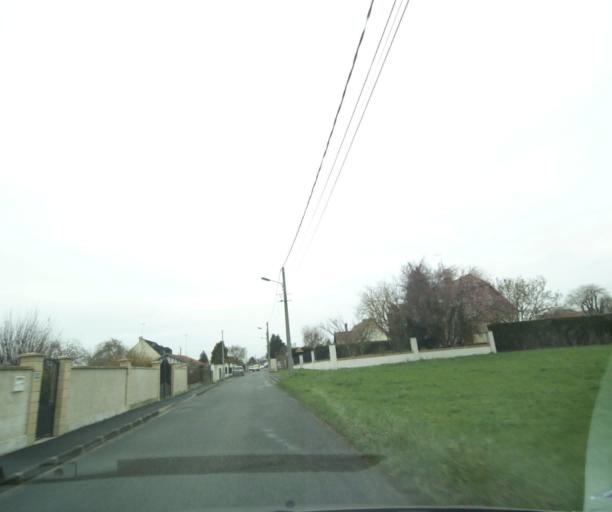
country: FR
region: Picardie
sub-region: Departement de l'Oise
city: Noyon
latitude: 49.5718
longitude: 3.0131
